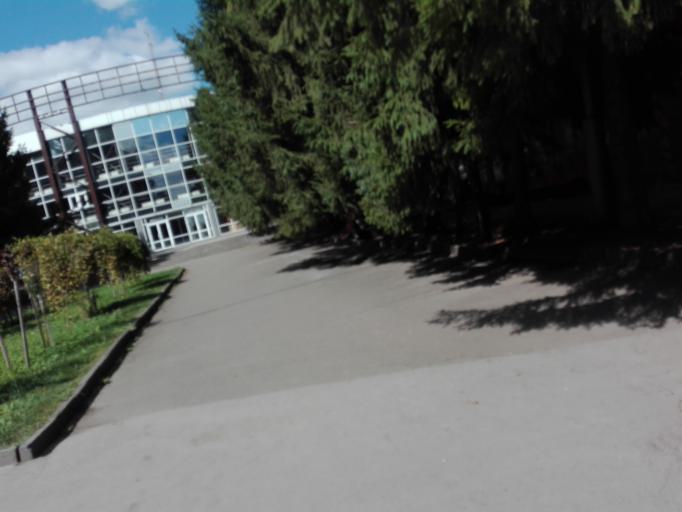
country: RU
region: Lipetsk
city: Lipetsk
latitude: 52.6188
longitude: 39.5921
